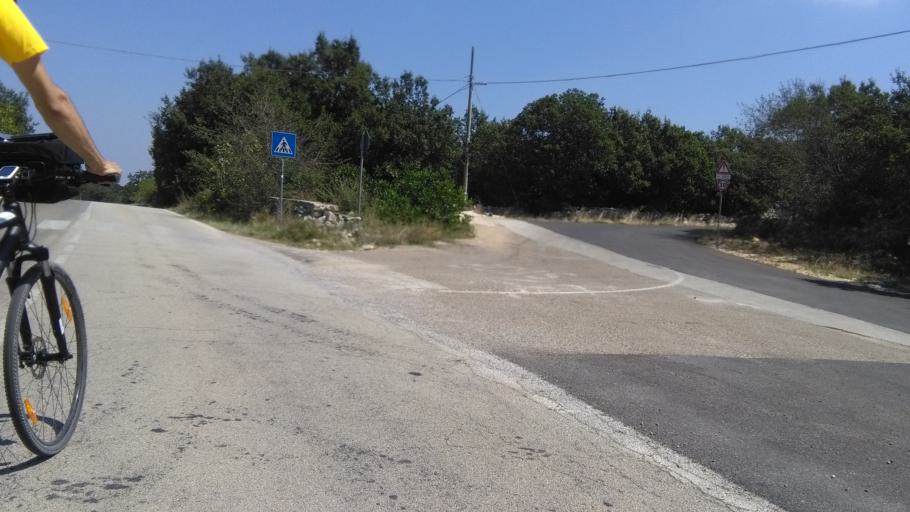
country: IT
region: Apulia
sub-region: Provincia di Bari
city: Noci
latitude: 40.8068
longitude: 17.1823
